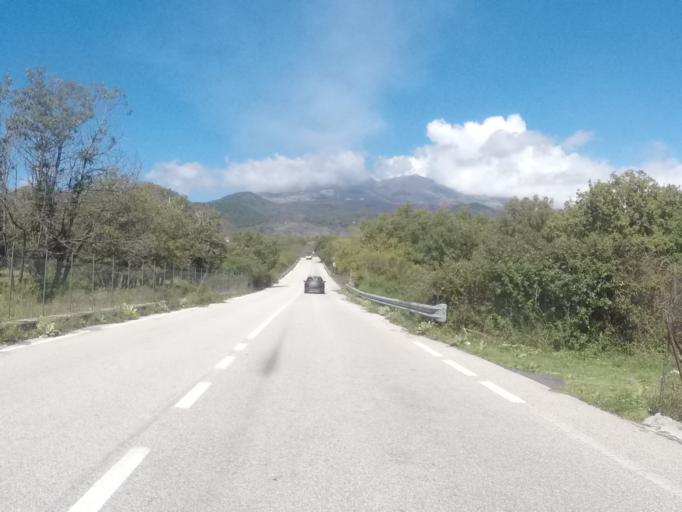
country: IT
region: Sicily
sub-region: Catania
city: Ragalna
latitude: 37.6462
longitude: 14.9880
